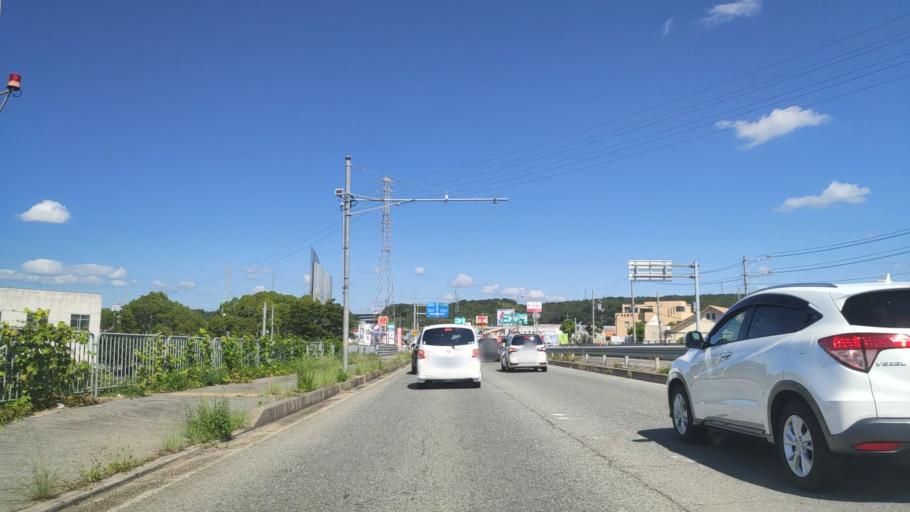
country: JP
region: Hyogo
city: Miki
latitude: 34.8023
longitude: 134.9656
